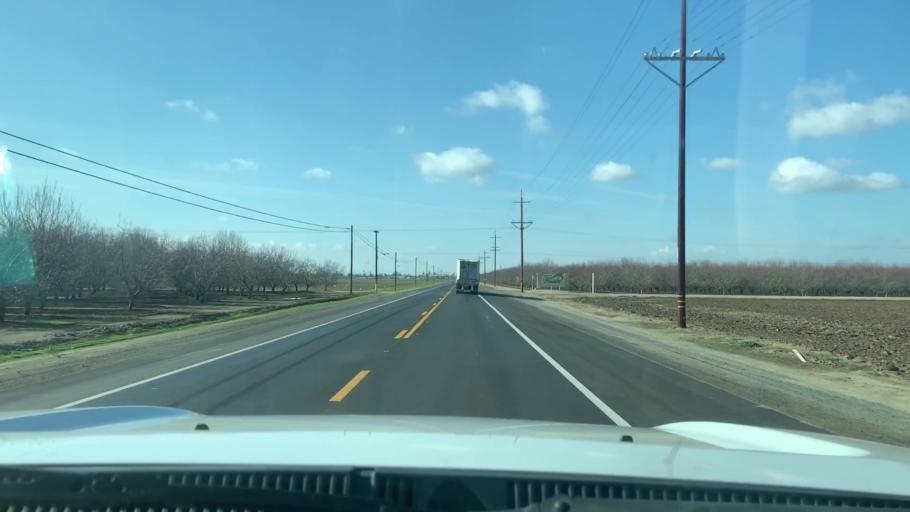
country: US
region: California
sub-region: Kern County
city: Wasco
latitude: 35.6016
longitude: -119.3113
